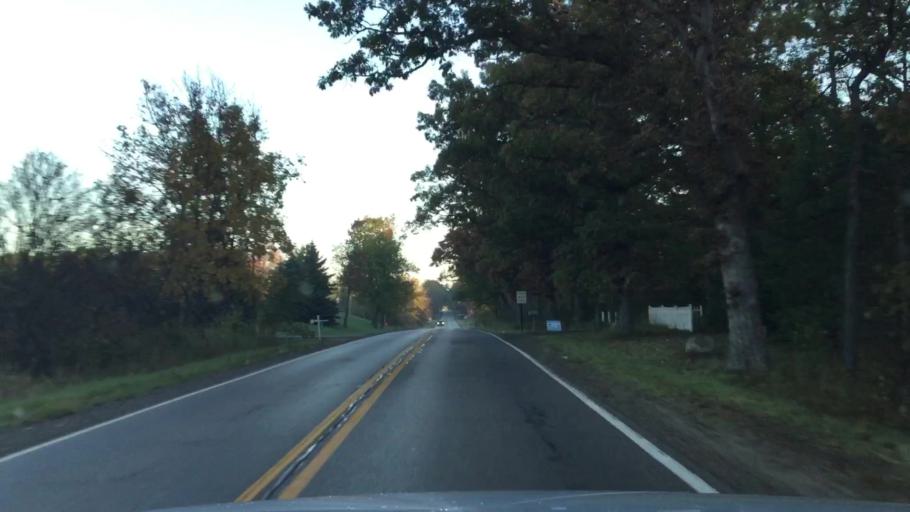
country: US
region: Michigan
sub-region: Livingston County
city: Howell
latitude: 42.7023
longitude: -83.9476
